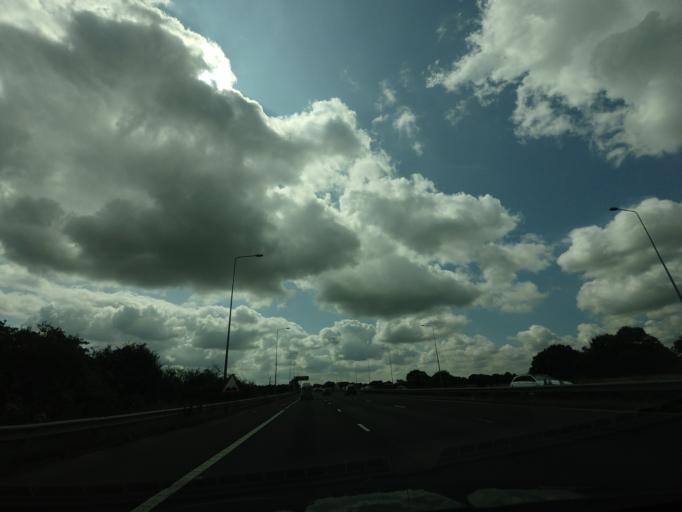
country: GB
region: England
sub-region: Borough of Wigan
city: Shevington
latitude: 53.6041
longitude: -2.6901
